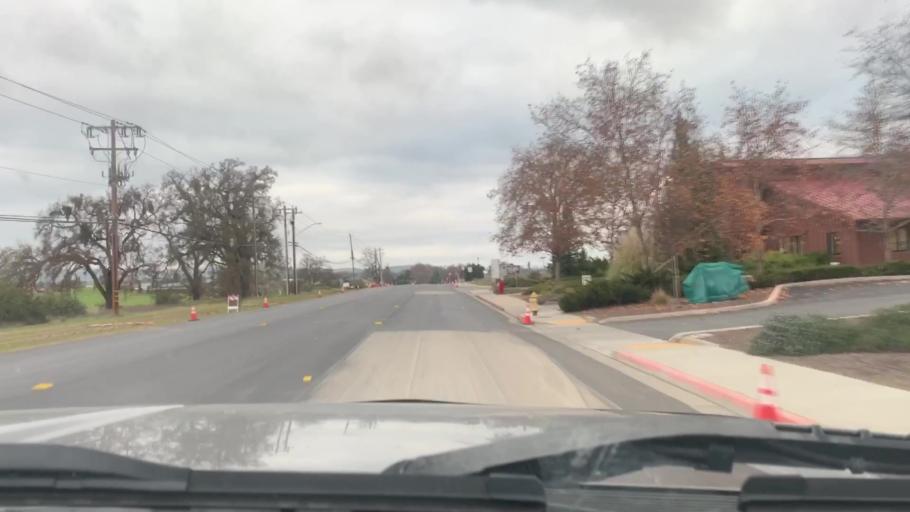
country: US
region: California
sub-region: San Luis Obispo County
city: Templeton
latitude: 35.5571
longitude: -120.7012
